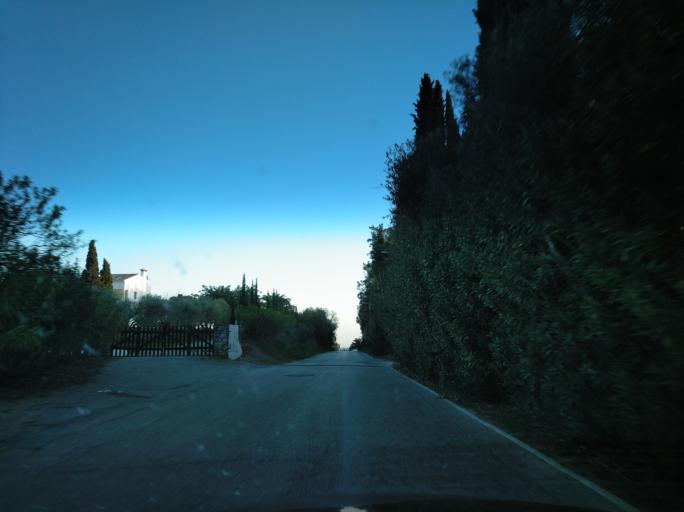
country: PT
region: Faro
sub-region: Tavira
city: Tavira
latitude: 37.1566
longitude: -7.5538
